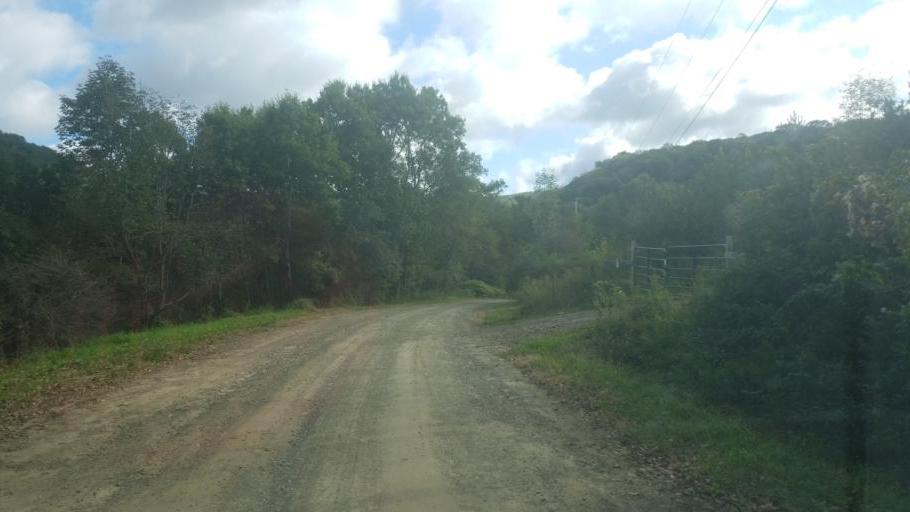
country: US
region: New York
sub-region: Allegany County
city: Cuba
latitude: 42.1508
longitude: -78.2943
